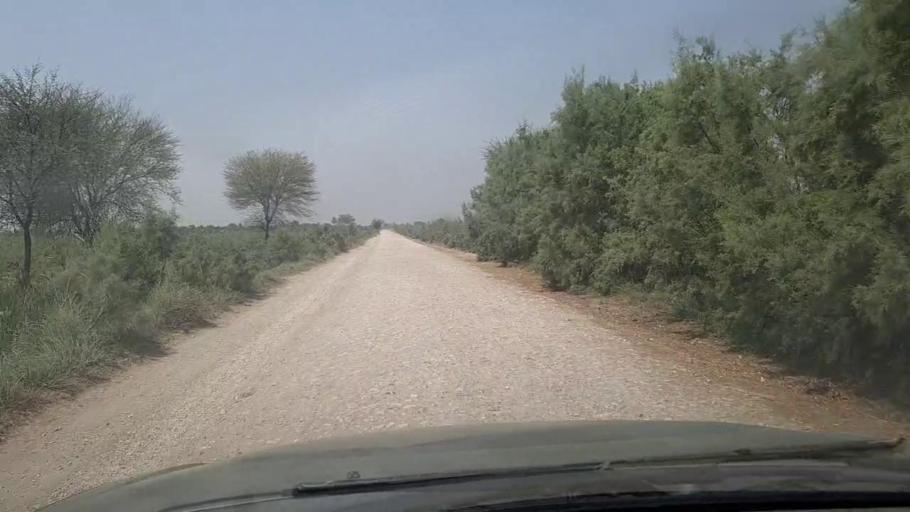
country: PK
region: Sindh
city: Adilpur
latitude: 27.9363
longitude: 69.2840
